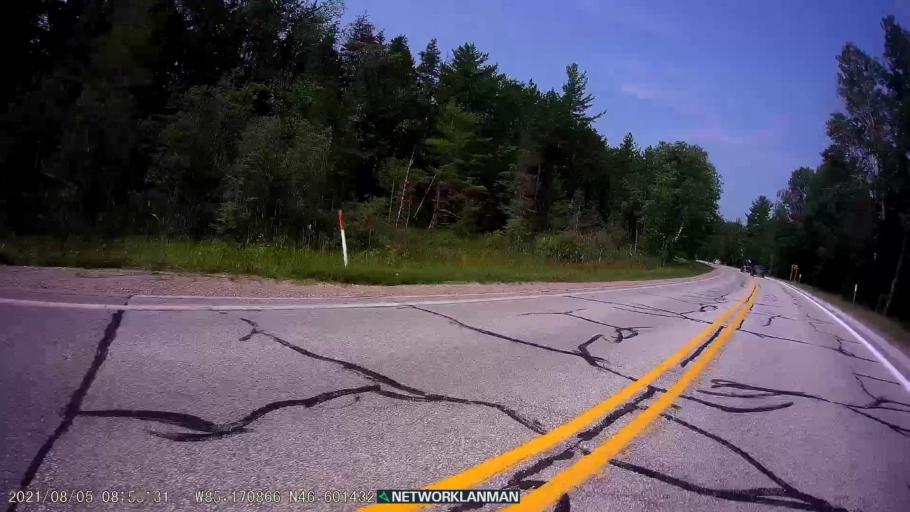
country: US
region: Michigan
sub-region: Luce County
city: Newberry
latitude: 46.6020
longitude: -85.1719
